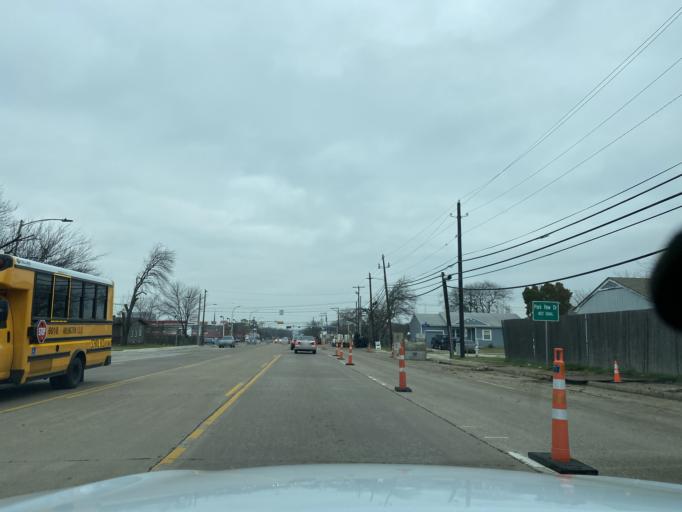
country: US
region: Texas
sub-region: Tarrant County
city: Arlington
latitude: 32.7196
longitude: -97.0974
